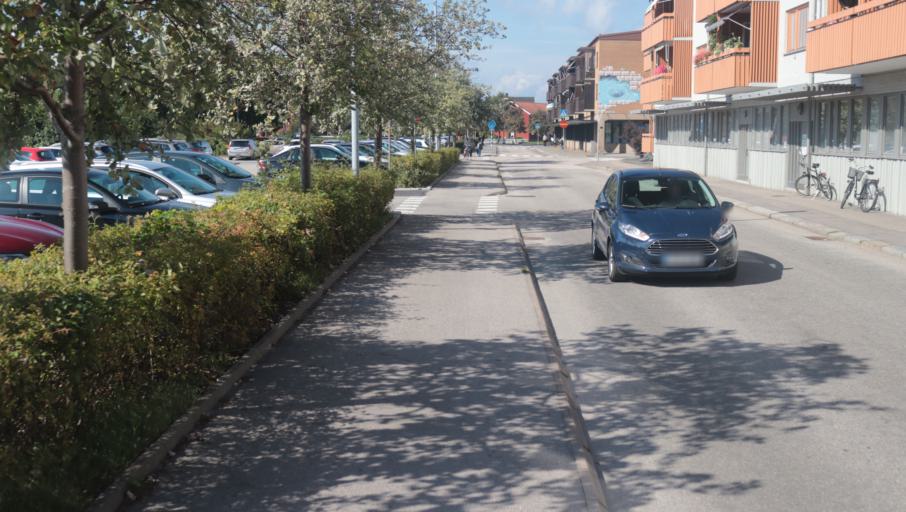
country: SE
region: Blekinge
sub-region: Karlshamns Kommun
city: Karlshamn
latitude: 56.1721
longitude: 14.8588
